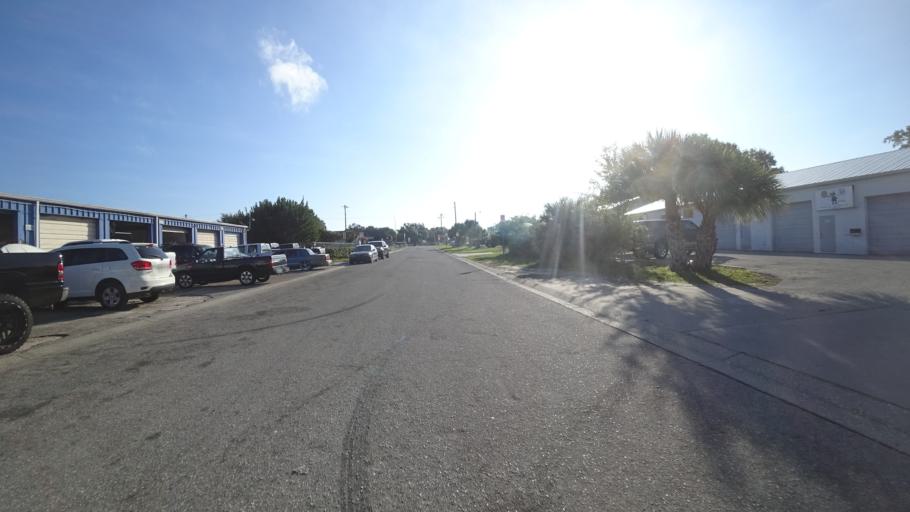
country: US
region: Florida
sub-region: Manatee County
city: West Samoset
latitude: 27.4716
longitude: -82.5645
